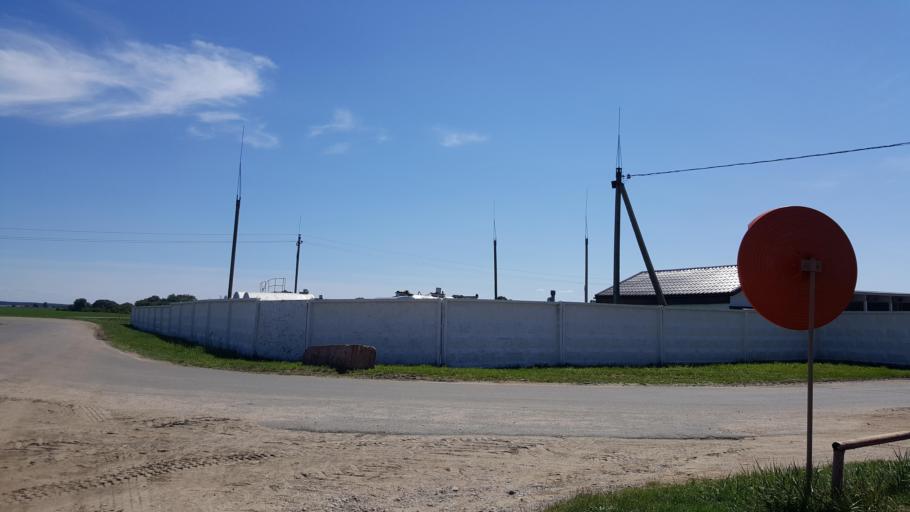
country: BY
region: Brest
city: Charnawchytsy
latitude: 52.2176
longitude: 23.7466
